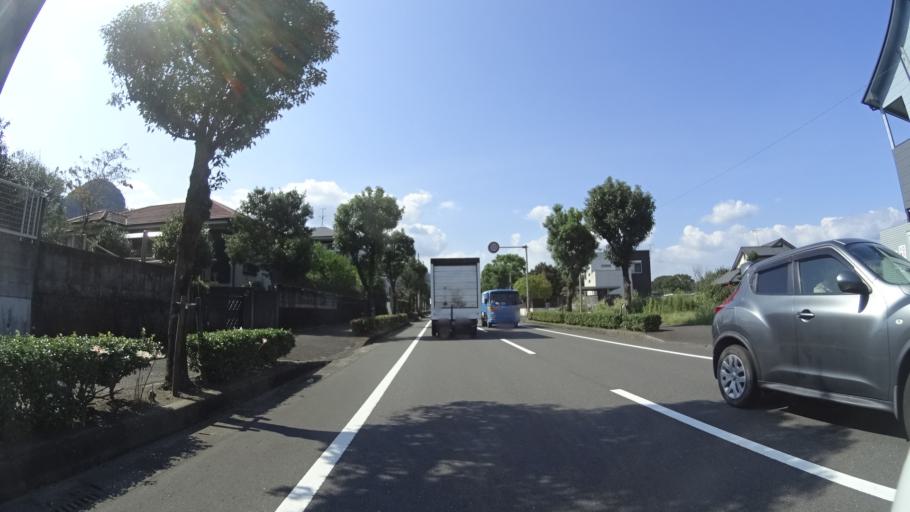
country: JP
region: Kagoshima
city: Kajiki
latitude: 31.7074
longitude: 130.6075
